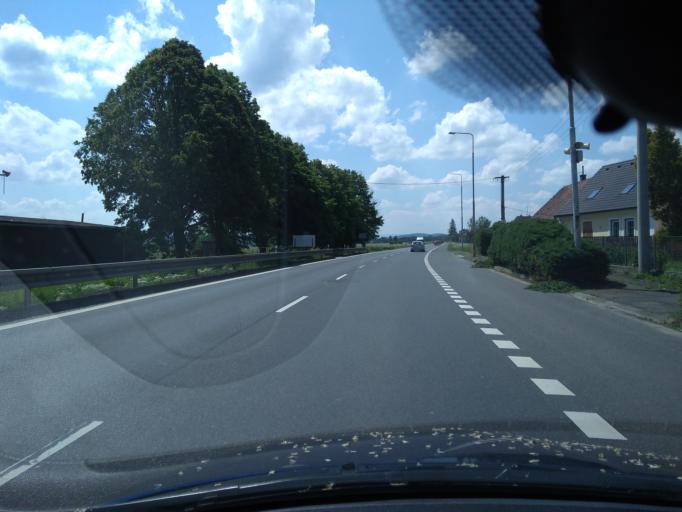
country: CZ
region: Plzensky
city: Svihov
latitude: 49.4988
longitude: 13.2924
